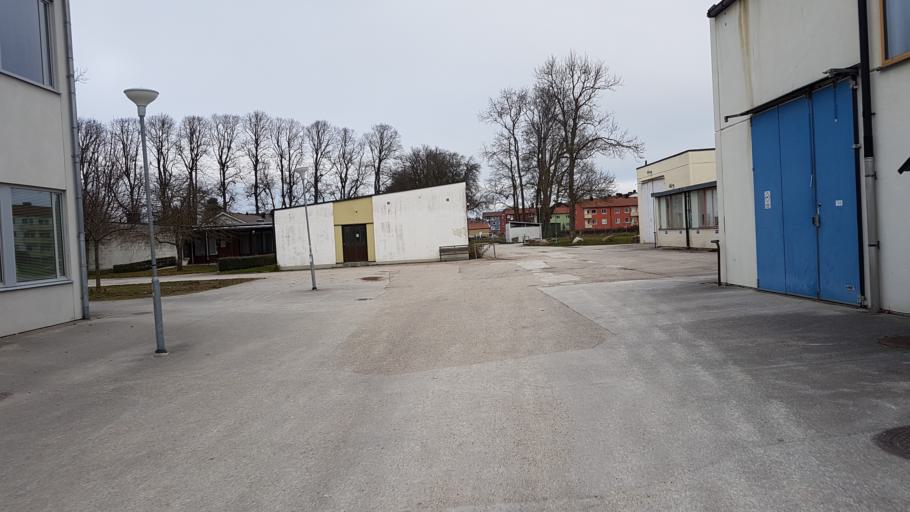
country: SE
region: Gotland
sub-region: Gotland
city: Visby
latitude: 57.6254
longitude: 18.2963
